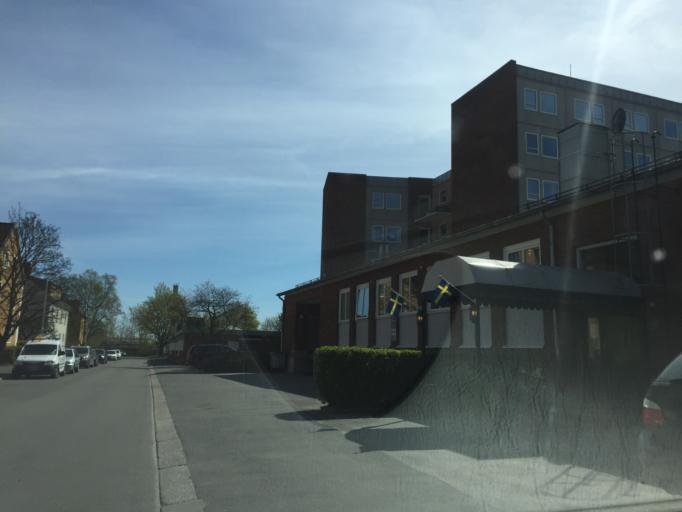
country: SE
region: OErebro
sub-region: Orebro Kommun
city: Orebro
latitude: 59.2671
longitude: 15.2299
